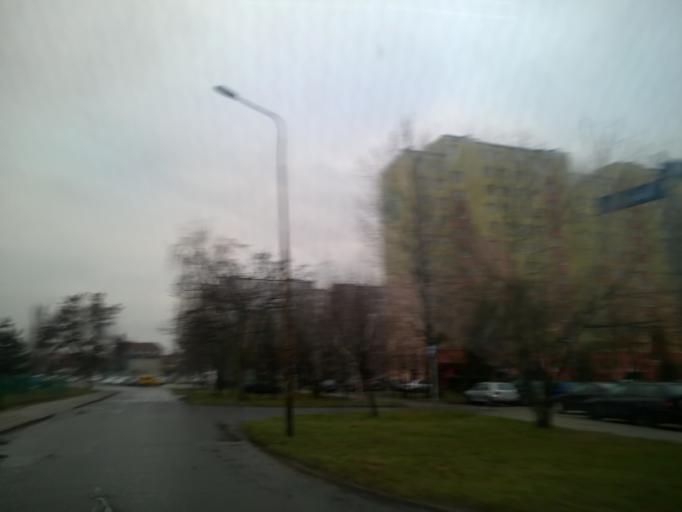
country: PL
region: Lower Silesian Voivodeship
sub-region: Powiat wroclawski
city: Wroclaw
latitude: 51.0782
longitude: 17.0468
